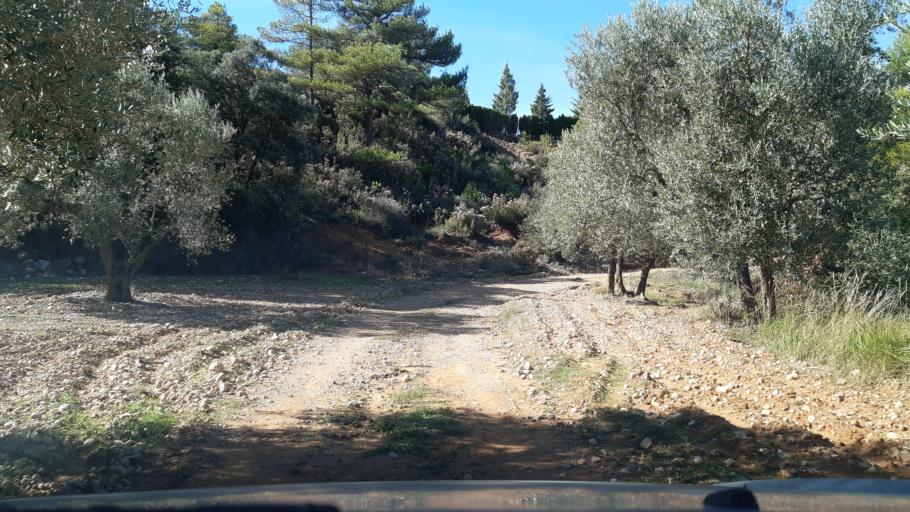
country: ES
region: Aragon
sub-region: Provincia de Teruel
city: Valderrobres
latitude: 40.8393
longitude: 0.2008
